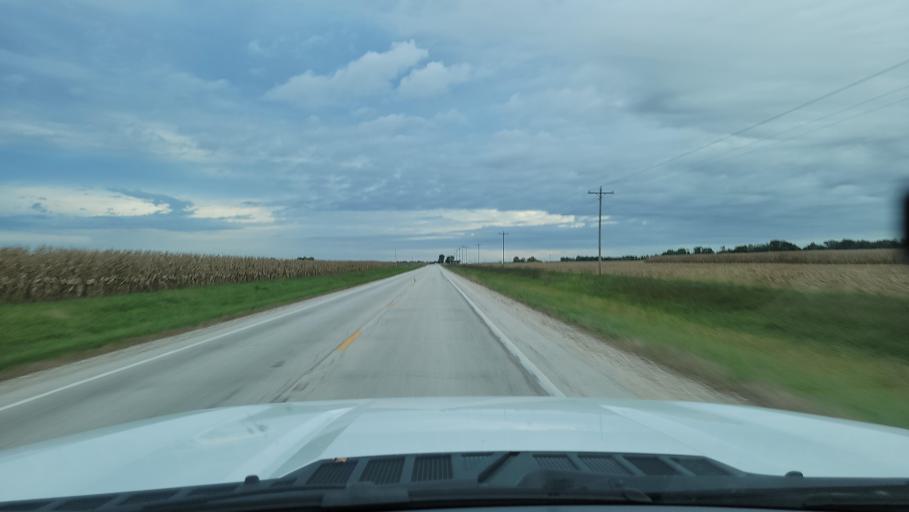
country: US
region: Illinois
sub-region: Schuyler County
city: Rushville
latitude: 40.0686
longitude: -90.6152
